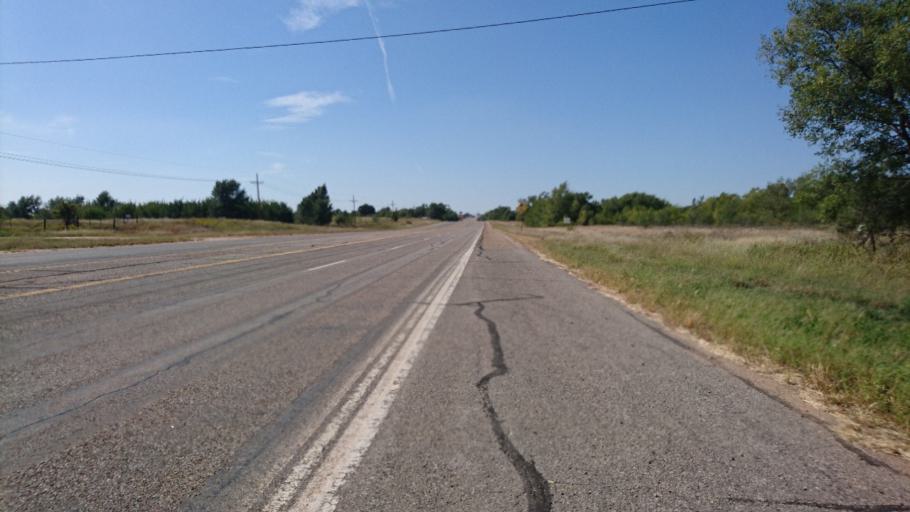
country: US
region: Texas
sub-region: Wheeler County
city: Shamrock
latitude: 35.2267
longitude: -100.2287
